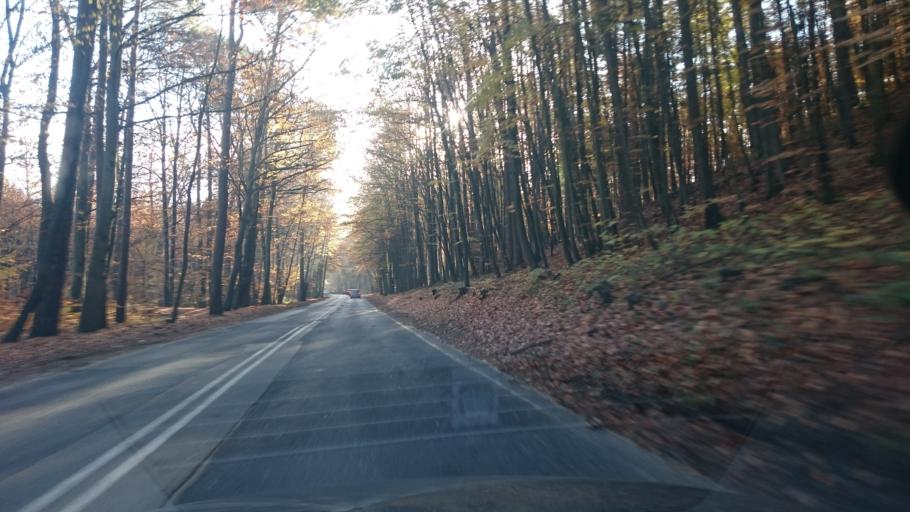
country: PL
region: Pomeranian Voivodeship
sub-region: Gdynia
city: Wielki Kack
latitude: 54.4569
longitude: 18.5140
